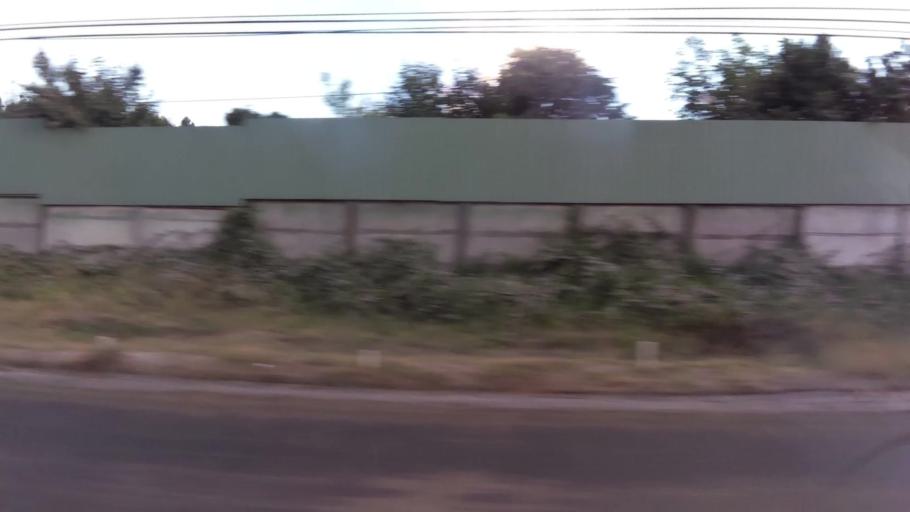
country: CL
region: Biobio
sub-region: Provincia de Concepcion
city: Concepcion
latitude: -36.8662
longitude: -73.0364
